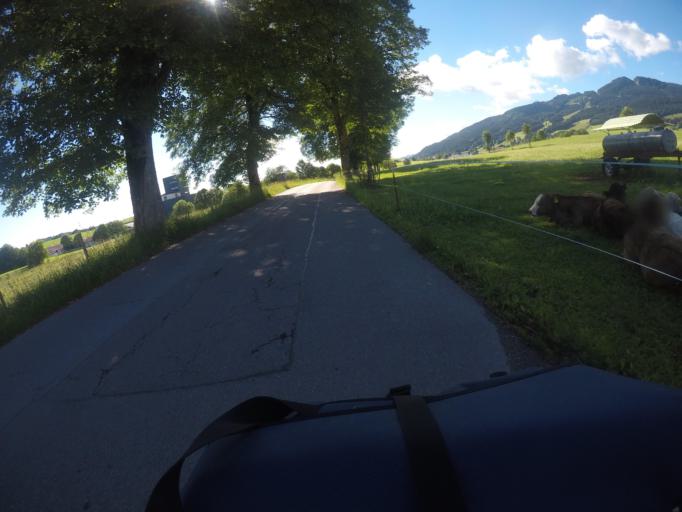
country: DE
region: Bavaria
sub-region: Swabia
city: Nesselwang
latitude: 47.6280
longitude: 10.4841
